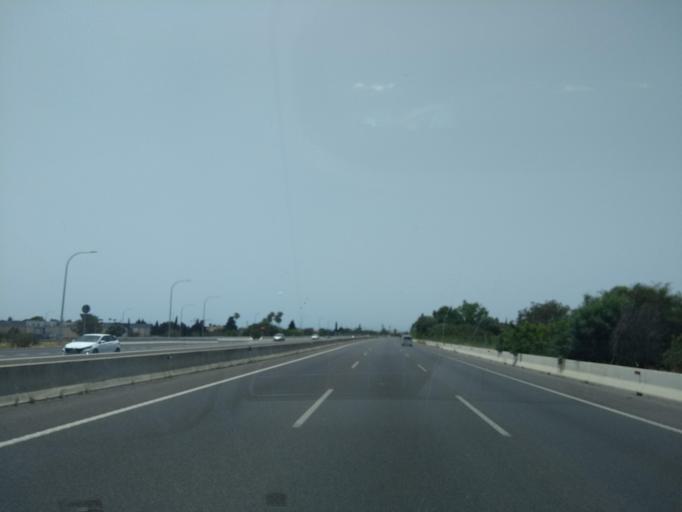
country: ES
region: Balearic Islands
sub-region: Illes Balears
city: Marratxi
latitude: 39.6252
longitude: 2.7138
